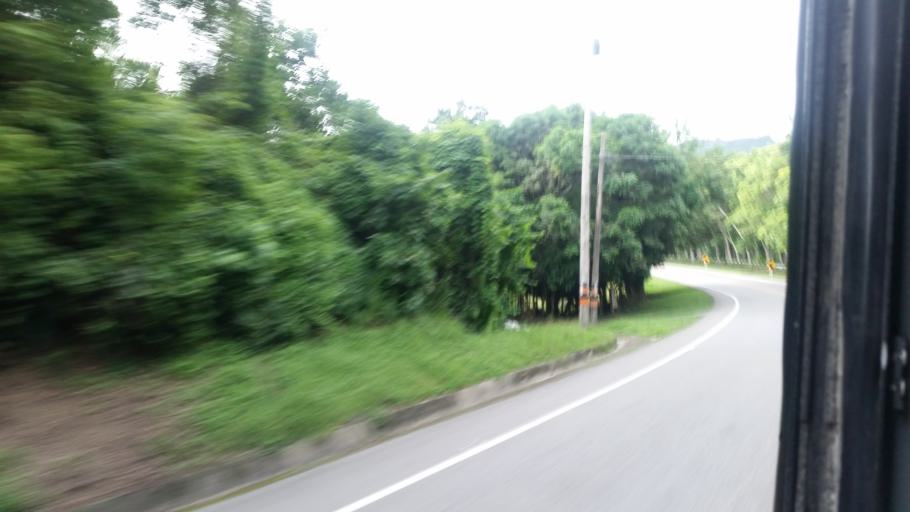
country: CO
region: Magdalena
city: Santa Marta
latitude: 11.2709
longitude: -73.8635
